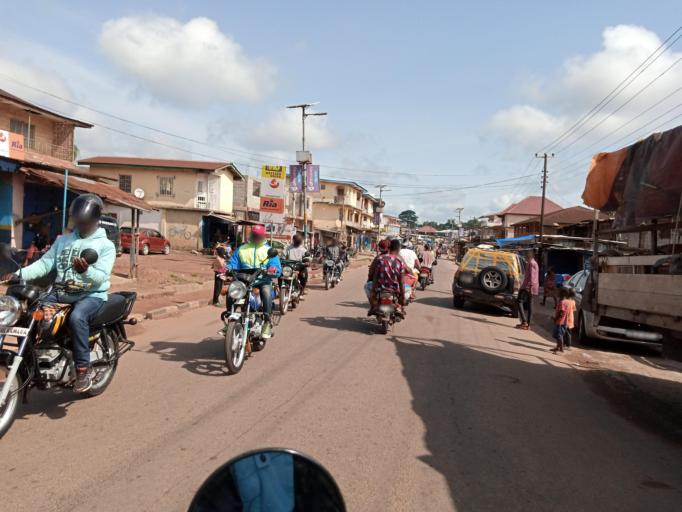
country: SL
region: Southern Province
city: Bo
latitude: 7.9644
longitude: -11.7351
